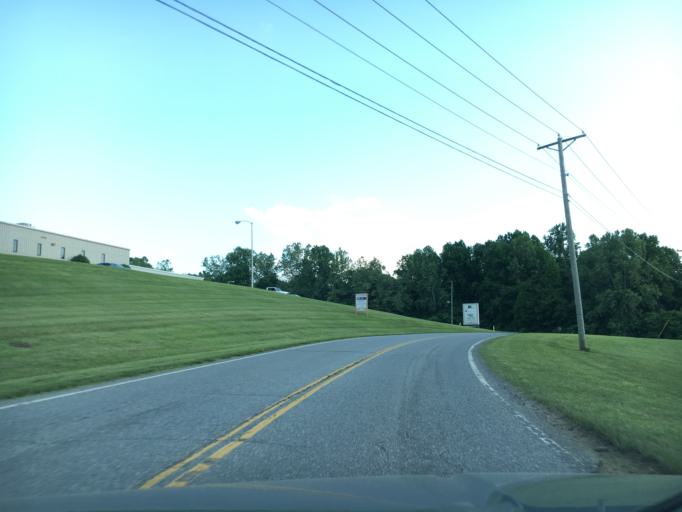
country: US
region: Virginia
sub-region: Bedford County
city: Forest
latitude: 37.3769
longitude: -79.2520
